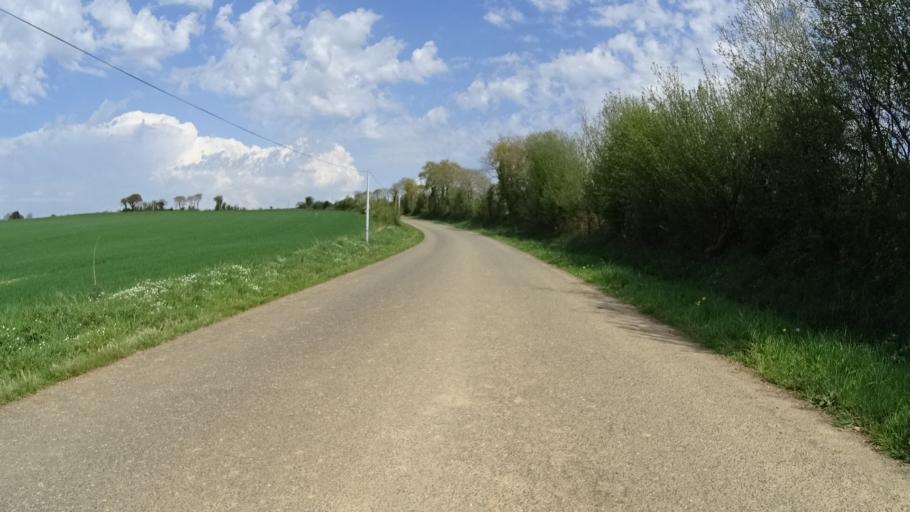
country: FR
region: Brittany
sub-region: Departement du Finistere
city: Sizun
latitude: 48.4263
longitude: -4.0832
